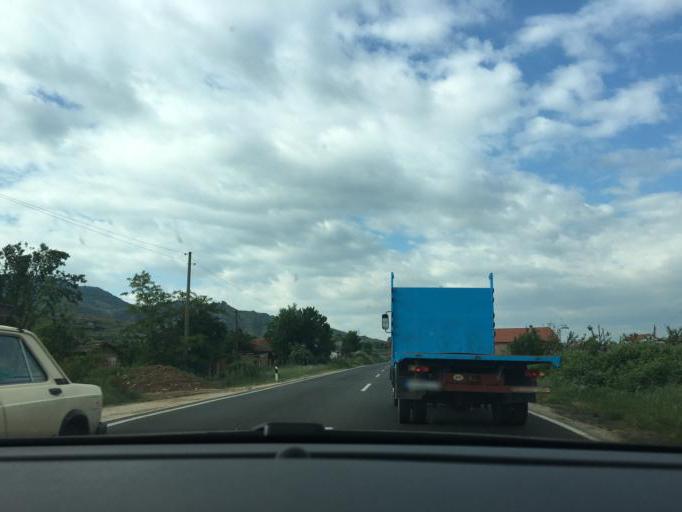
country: MK
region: Prilep
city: Prilep
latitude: 41.3443
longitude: 21.5750
